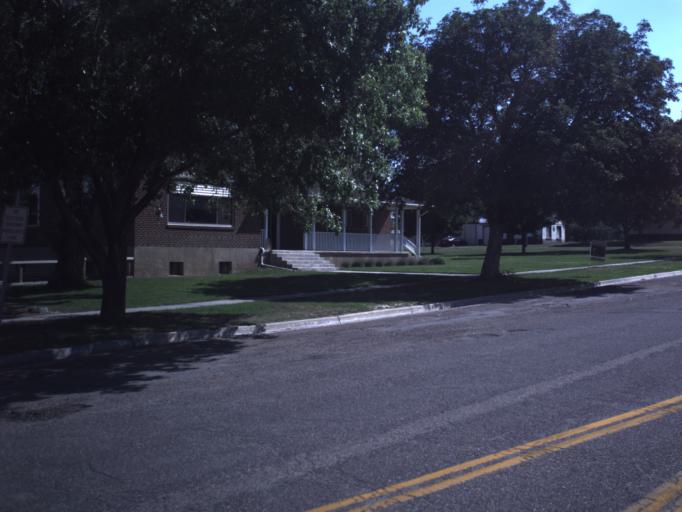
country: US
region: Utah
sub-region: Sanpete County
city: Mount Pleasant
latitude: 39.5467
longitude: -111.4544
